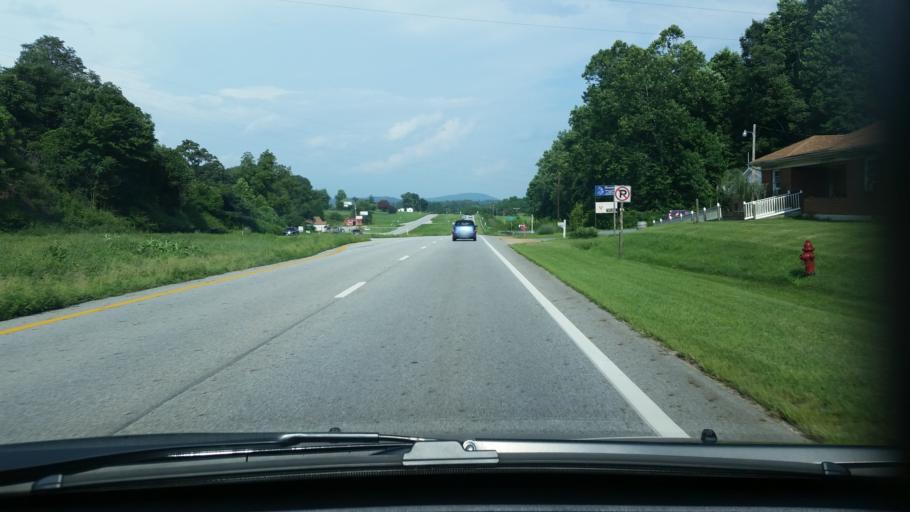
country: US
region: Virginia
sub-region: Nelson County
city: Lovingston
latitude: 37.7119
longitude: -78.9252
